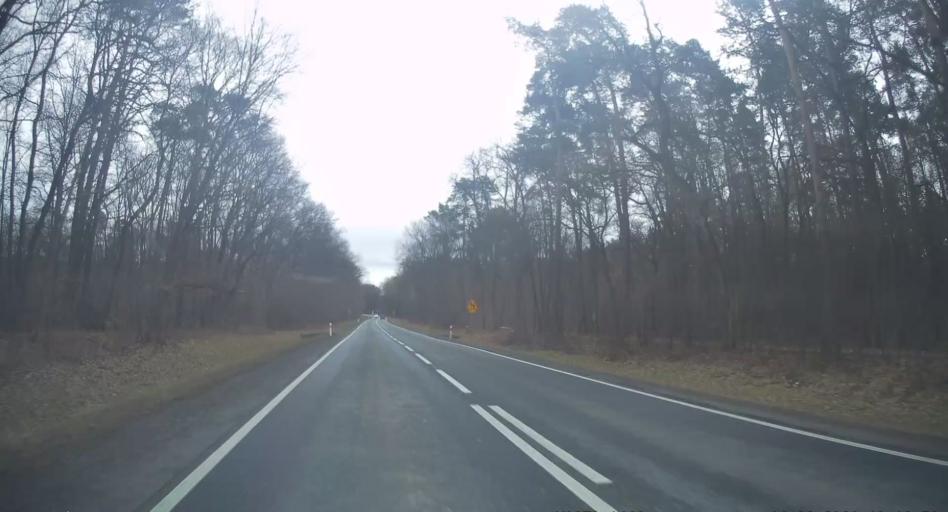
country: PL
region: Lesser Poland Voivodeship
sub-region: Powiat wielicki
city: Szarow
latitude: 50.0127
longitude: 20.2494
